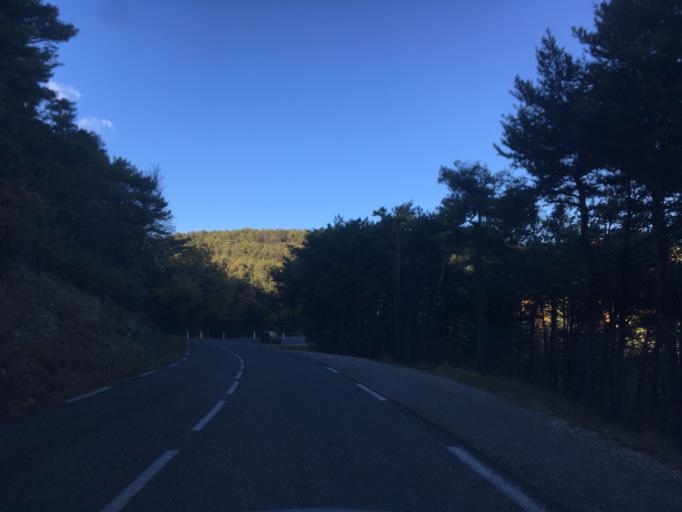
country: FR
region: Provence-Alpes-Cote d'Azur
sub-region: Departement du Var
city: Montferrat
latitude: 43.7206
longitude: 6.5016
